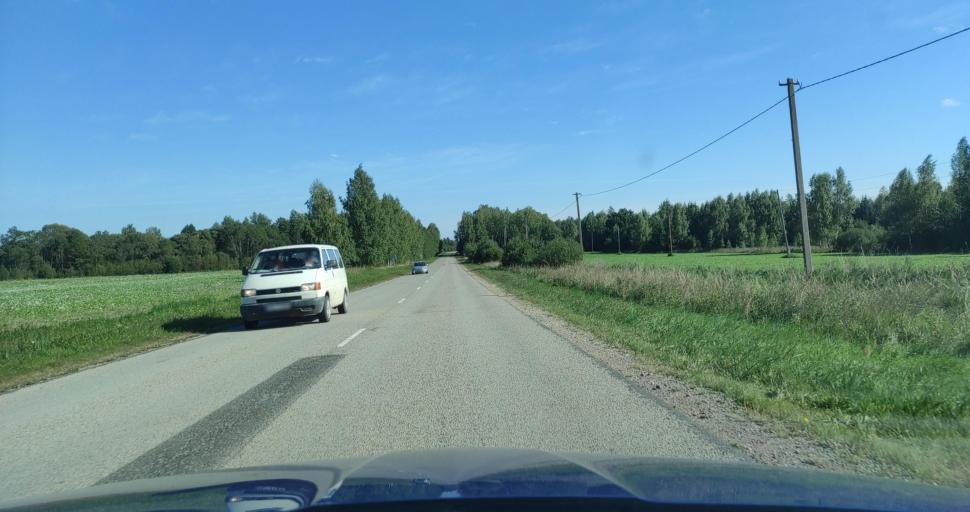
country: LV
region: Skrunda
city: Skrunda
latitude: 56.6819
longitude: 21.9072
